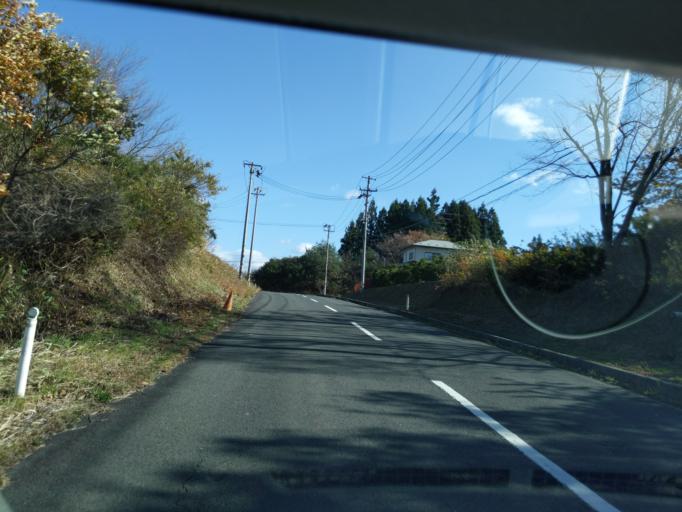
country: JP
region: Iwate
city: Mizusawa
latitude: 39.0274
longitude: 141.1126
